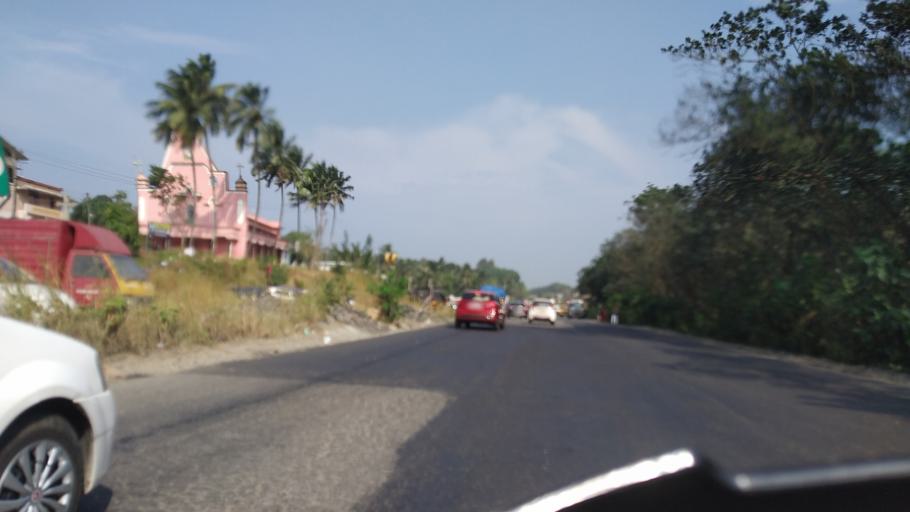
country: IN
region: Kerala
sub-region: Thrissur District
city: Chelakara
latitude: 10.5785
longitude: 76.4129
